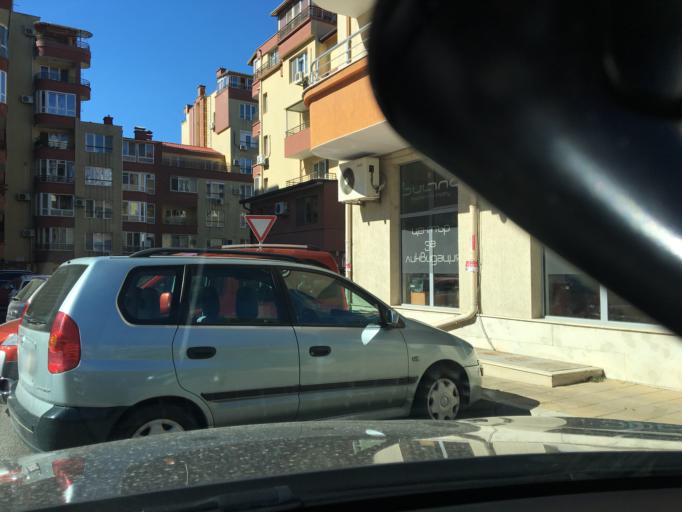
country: BG
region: Burgas
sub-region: Obshtina Burgas
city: Burgas
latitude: 42.5136
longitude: 27.4574
